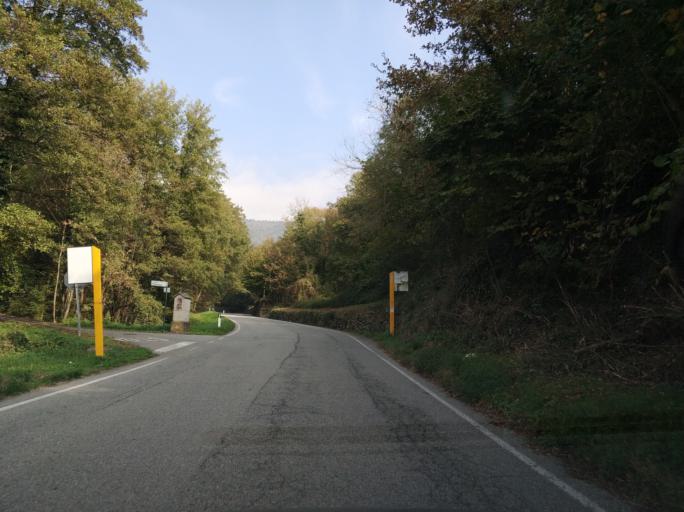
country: IT
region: Piedmont
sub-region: Provincia di Torino
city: Chiaverano
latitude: 45.5021
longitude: 7.8982
